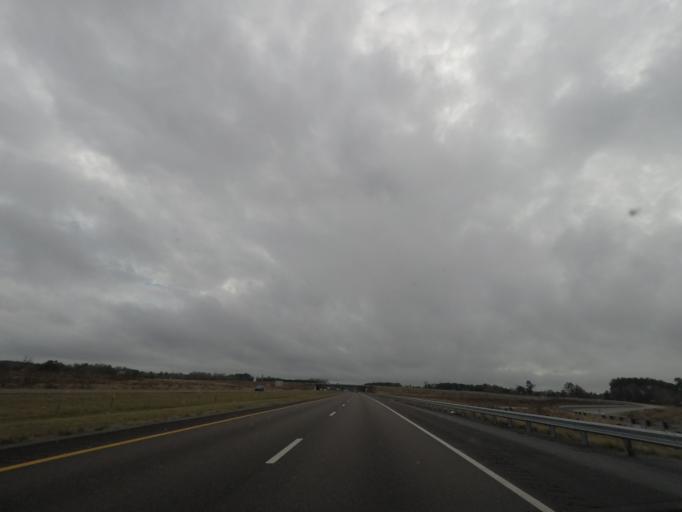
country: US
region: South Carolina
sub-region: Orangeburg County
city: Holly Hill
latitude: 33.4659
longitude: -80.4778
